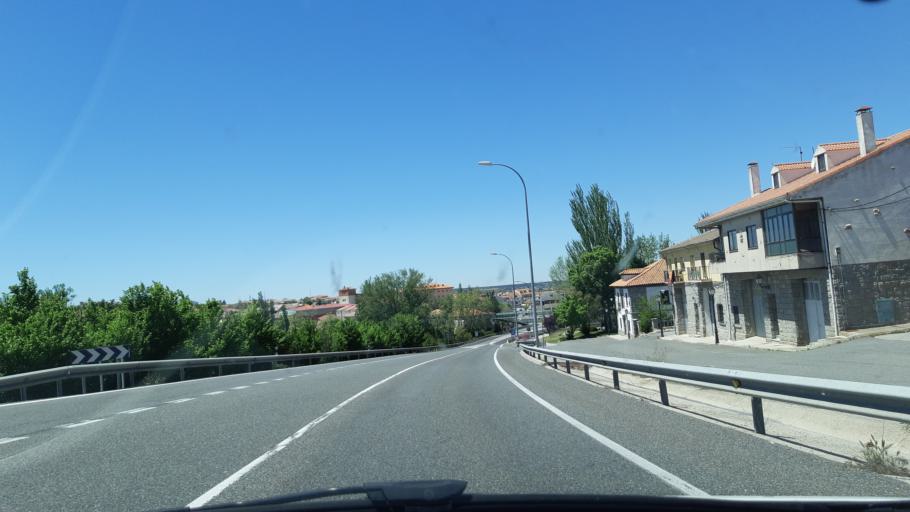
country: ES
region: Castille and Leon
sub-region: Provincia de Segovia
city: Villacastin
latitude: 40.7782
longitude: -4.4061
